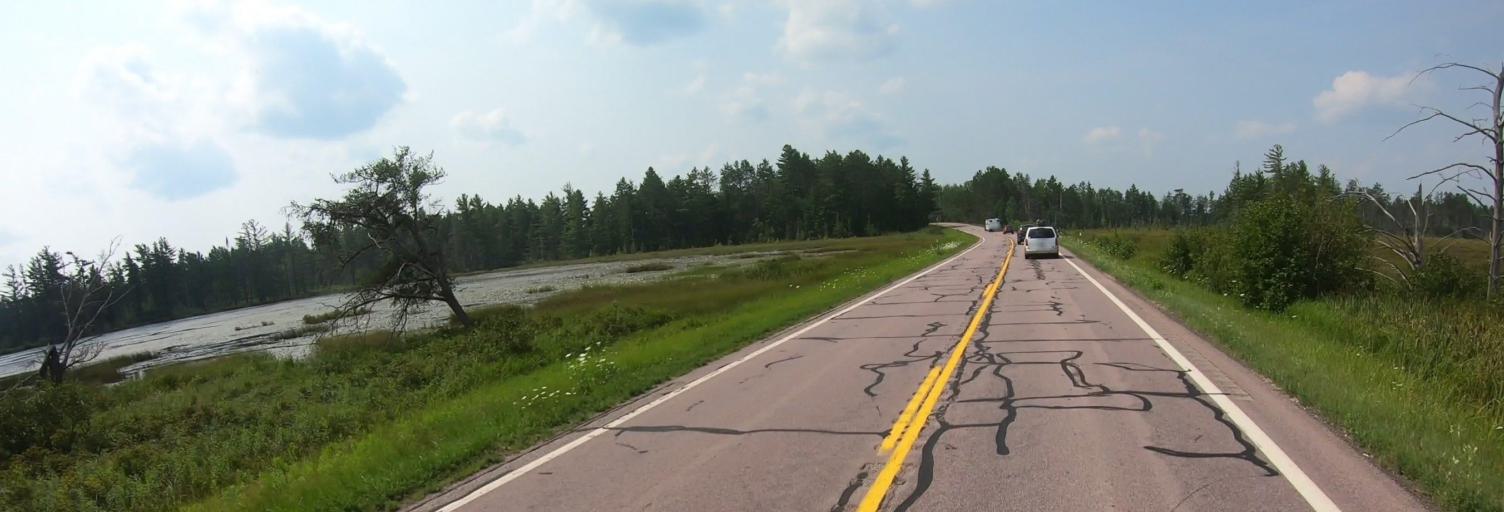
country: US
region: Michigan
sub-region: Luce County
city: Newberry
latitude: 46.4514
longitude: -85.4692
